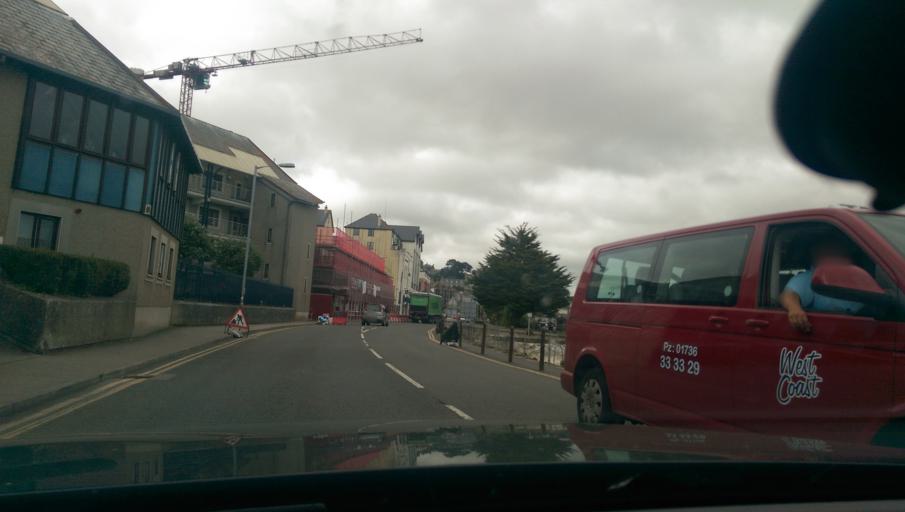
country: GB
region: England
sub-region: Cornwall
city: Penzance
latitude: 50.1186
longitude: -5.5334
